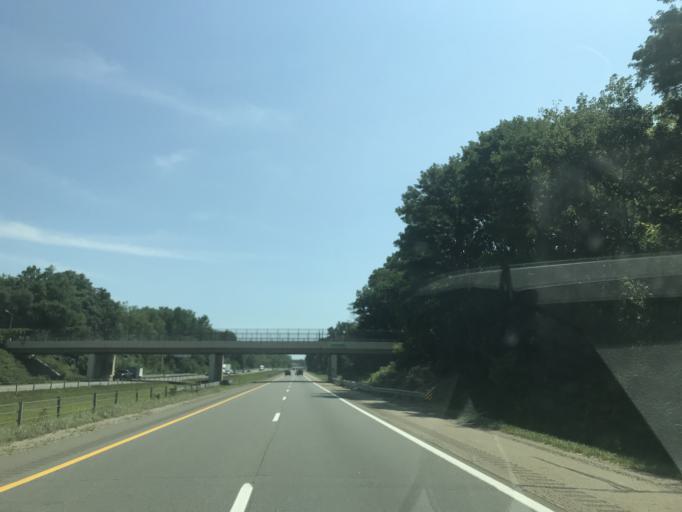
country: US
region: Michigan
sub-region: Kent County
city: Comstock Park
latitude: 43.0210
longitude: -85.6489
